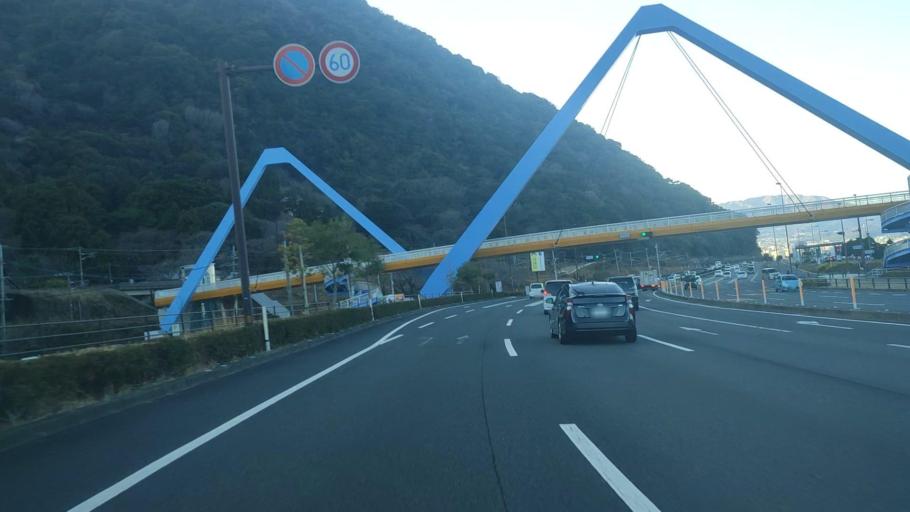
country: JP
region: Oita
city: Beppu
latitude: 33.2581
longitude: 131.5352
